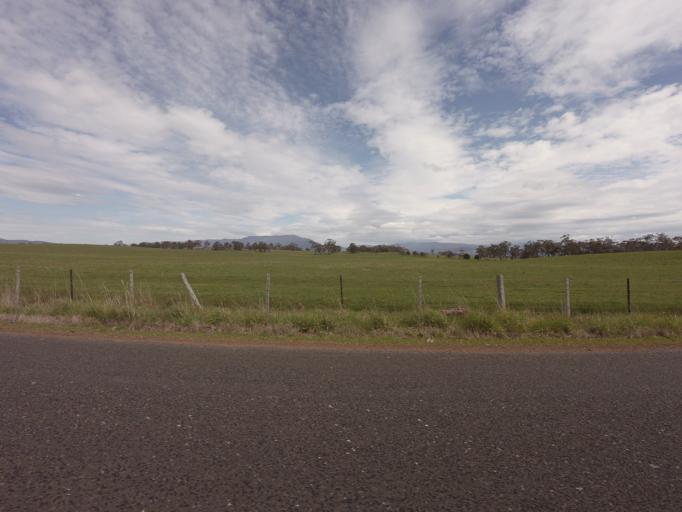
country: AU
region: Tasmania
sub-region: Northern Midlands
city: Evandale
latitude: -41.7875
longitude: 147.2430
